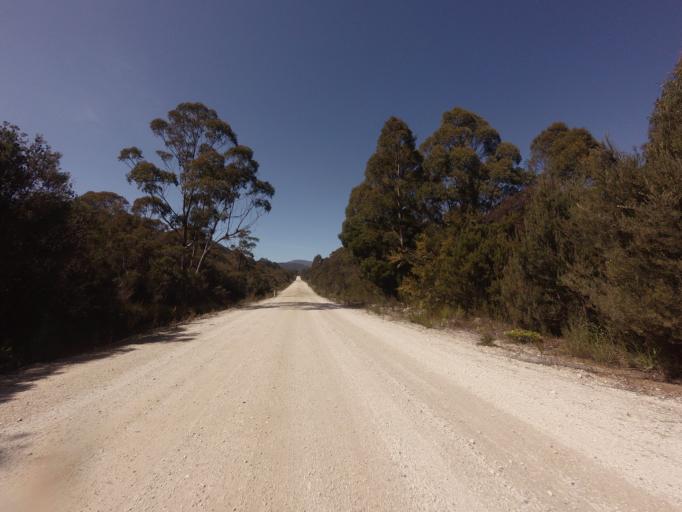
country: AU
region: Tasmania
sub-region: Huon Valley
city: Geeveston
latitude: -42.9447
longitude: 146.3500
